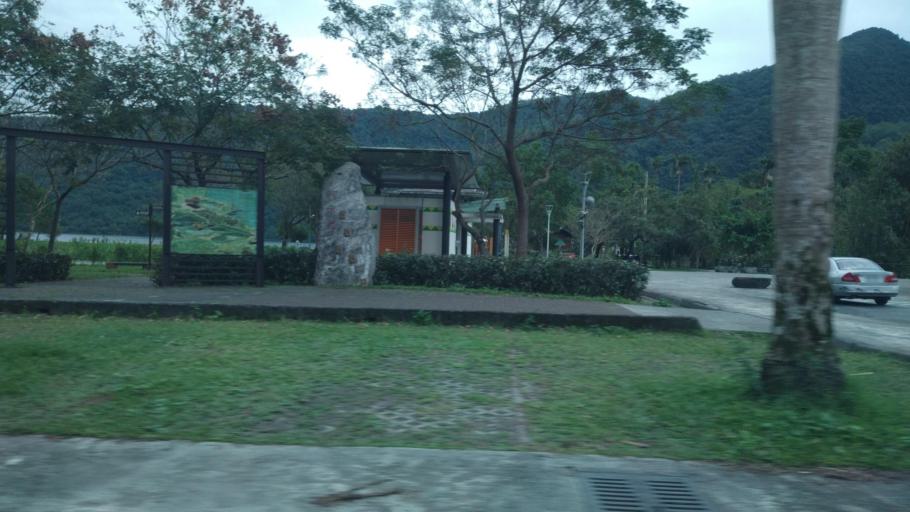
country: TW
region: Taiwan
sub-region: Hualien
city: Hualian
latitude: 23.9252
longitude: 121.5056
